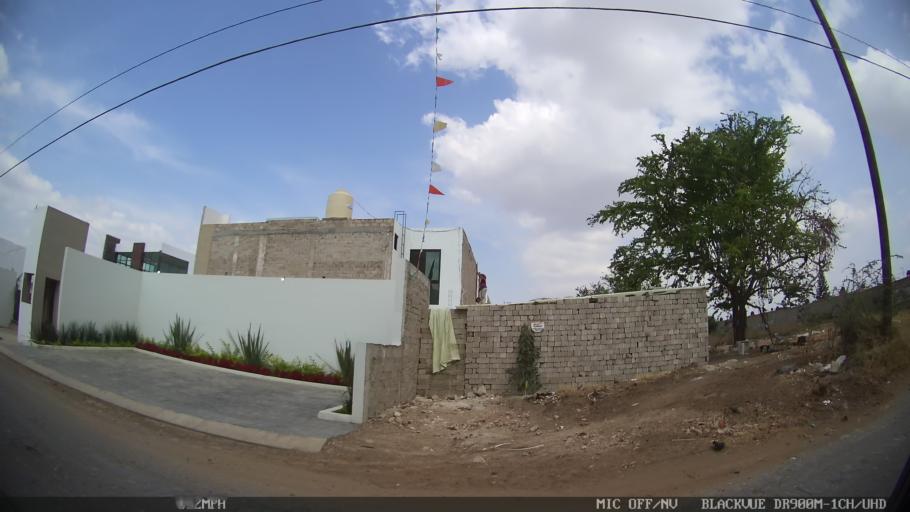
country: MX
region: Jalisco
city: Tonala
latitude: 20.6260
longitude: -103.2313
